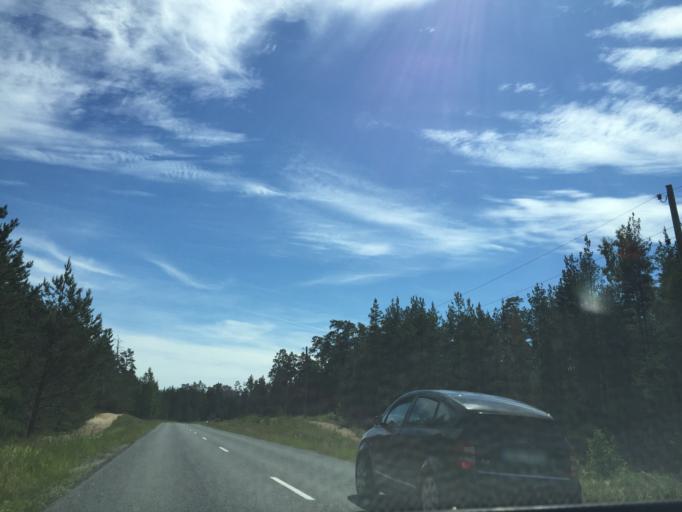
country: LV
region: Dundaga
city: Dundaga
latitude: 57.6458
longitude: 22.5716
